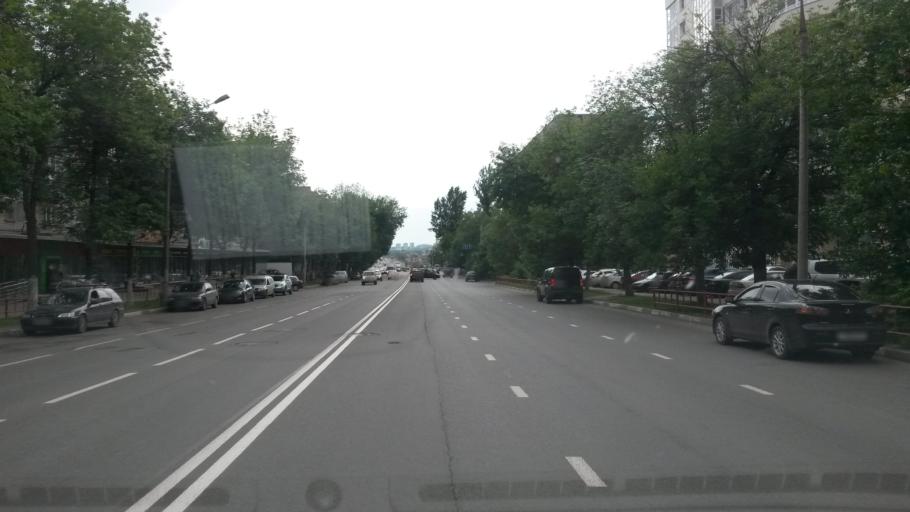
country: RU
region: Jaroslavl
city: Yaroslavl
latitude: 57.6232
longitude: 39.8580
